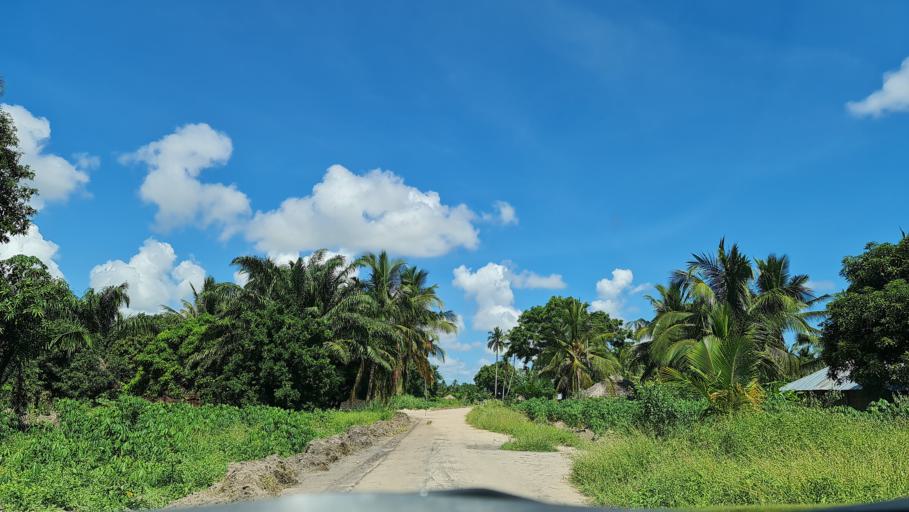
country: MZ
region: Zambezia
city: Quelimane
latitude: -17.3826
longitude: 37.5158
